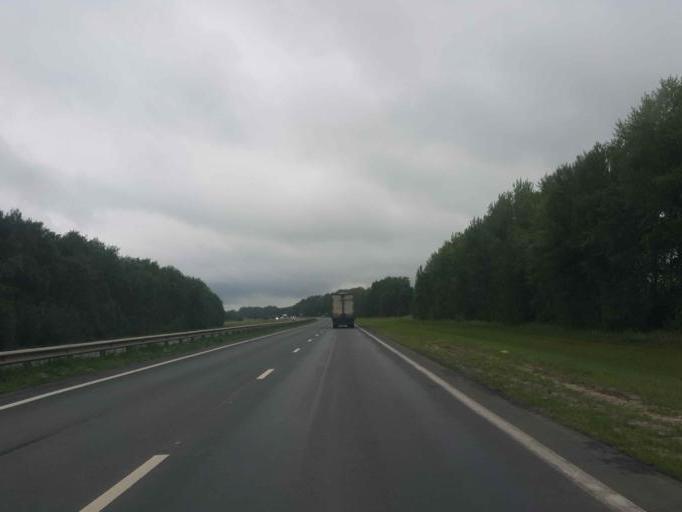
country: RU
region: Tambov
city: Selezni
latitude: 52.7656
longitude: 41.1055
